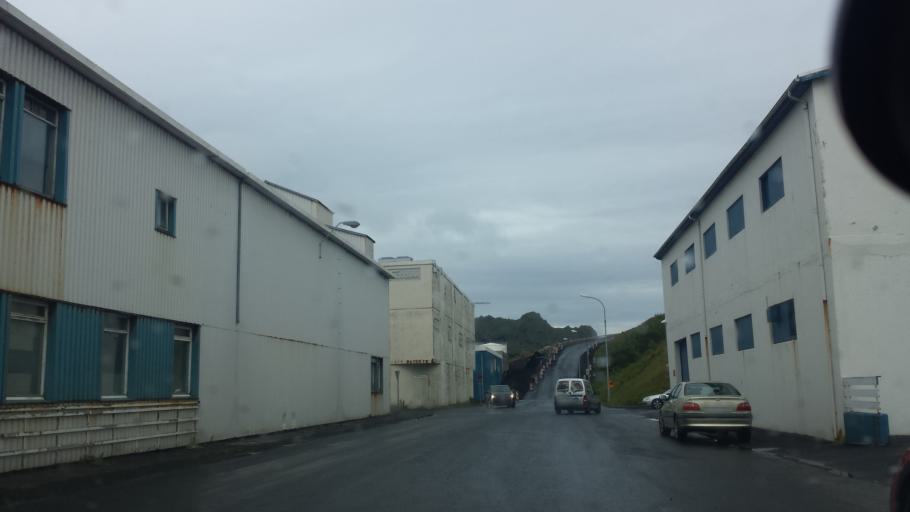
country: IS
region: South
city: Vestmannaeyjar
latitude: 63.4422
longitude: -20.2688
